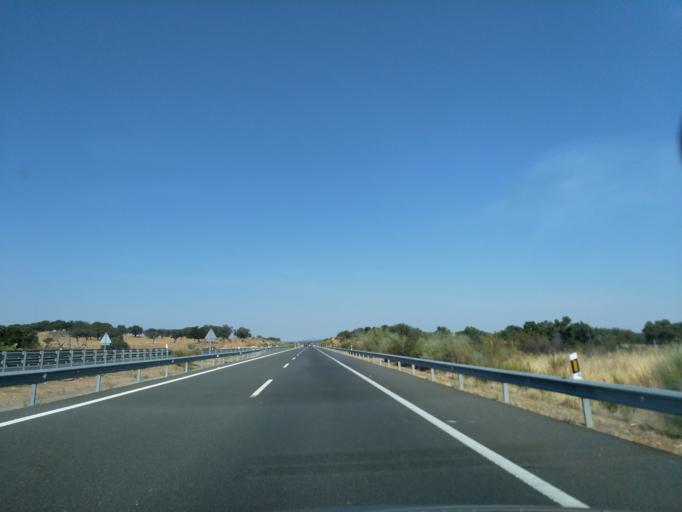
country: ES
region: Extremadura
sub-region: Provincia de Caceres
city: Casas de Don Antonio
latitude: 39.2005
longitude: -6.2810
